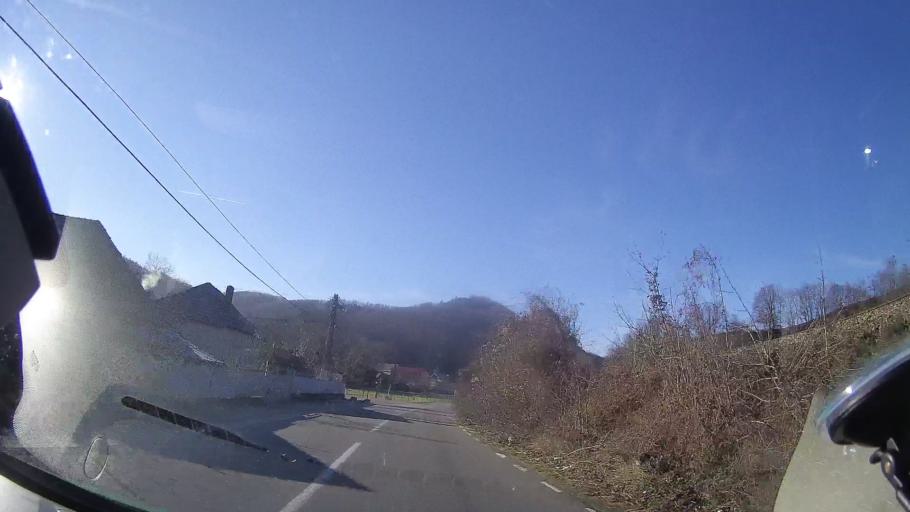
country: RO
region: Bihor
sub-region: Comuna Bratca
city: Bratca
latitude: 46.9211
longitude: 22.6231
